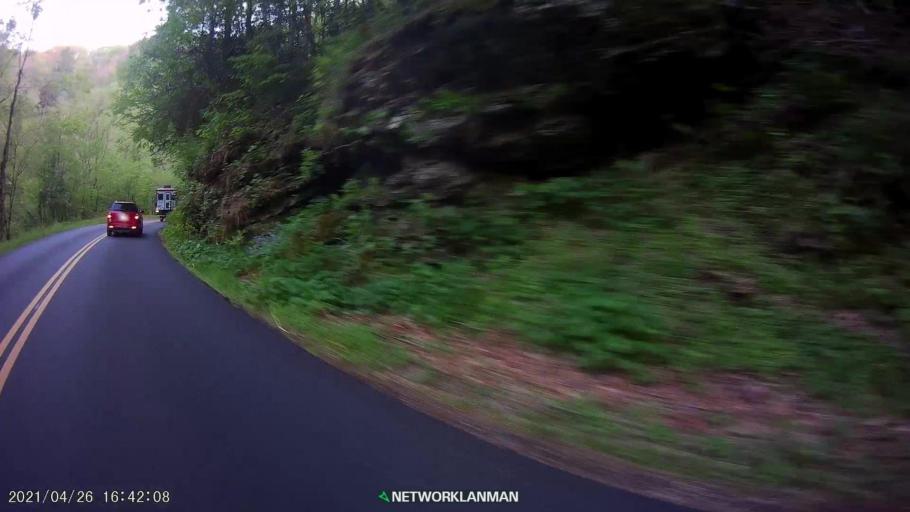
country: US
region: Tennessee
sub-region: Sevier County
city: Pigeon Forge
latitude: 35.6655
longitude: -83.6892
